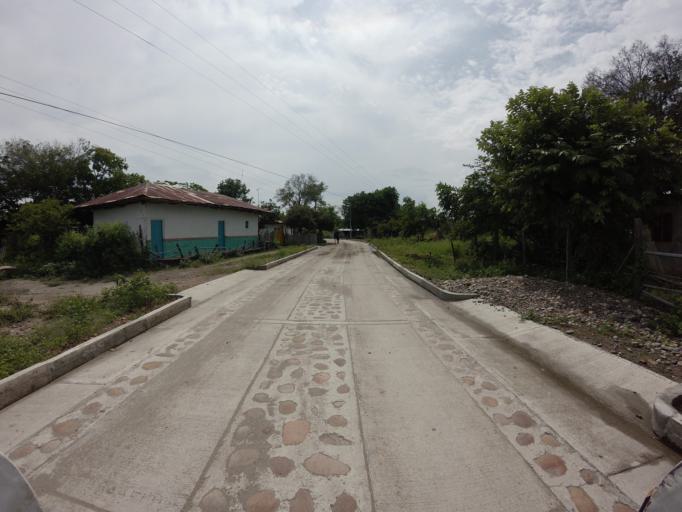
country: CO
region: Tolima
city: Natagaima
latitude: 3.4556
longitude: -75.1441
